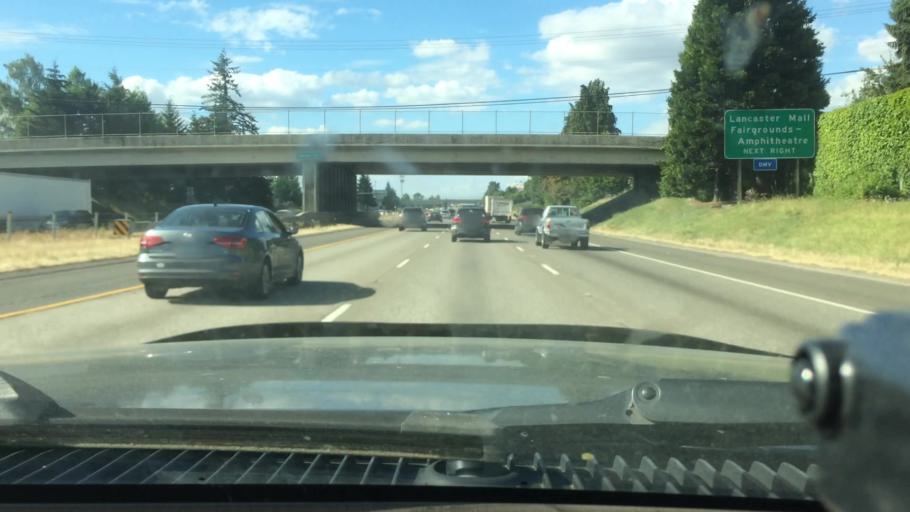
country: US
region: Oregon
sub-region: Marion County
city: Four Corners
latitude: 44.9391
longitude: -122.9901
